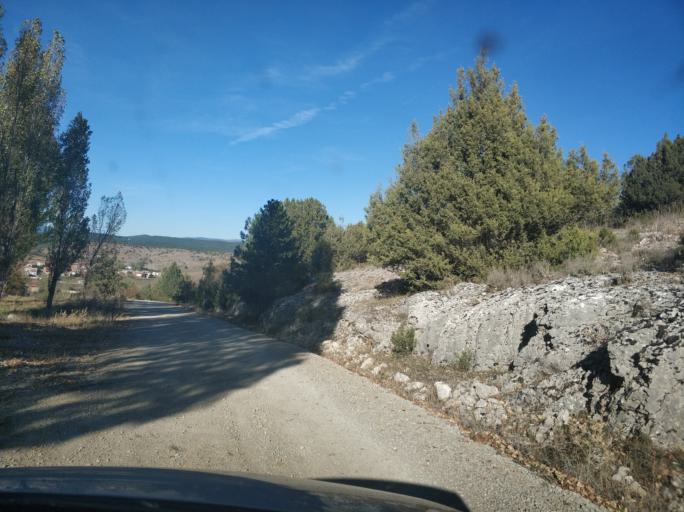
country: ES
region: Castille and Leon
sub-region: Provincia de Burgos
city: Hontoria del Pinar
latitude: 41.8407
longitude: -3.1645
